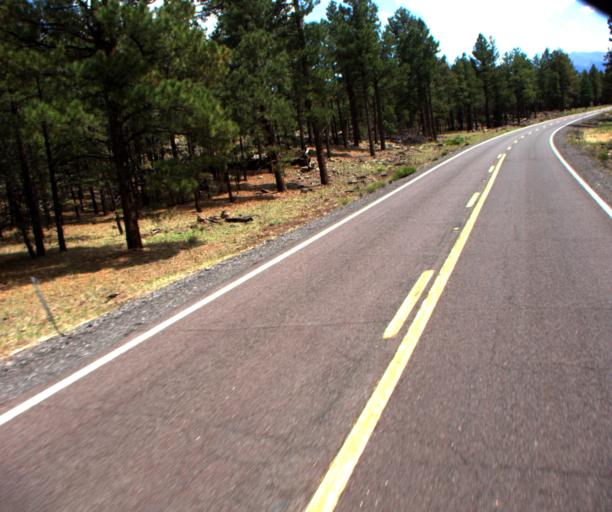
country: US
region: Arizona
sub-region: Coconino County
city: Parks
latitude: 35.4600
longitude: -111.7785
